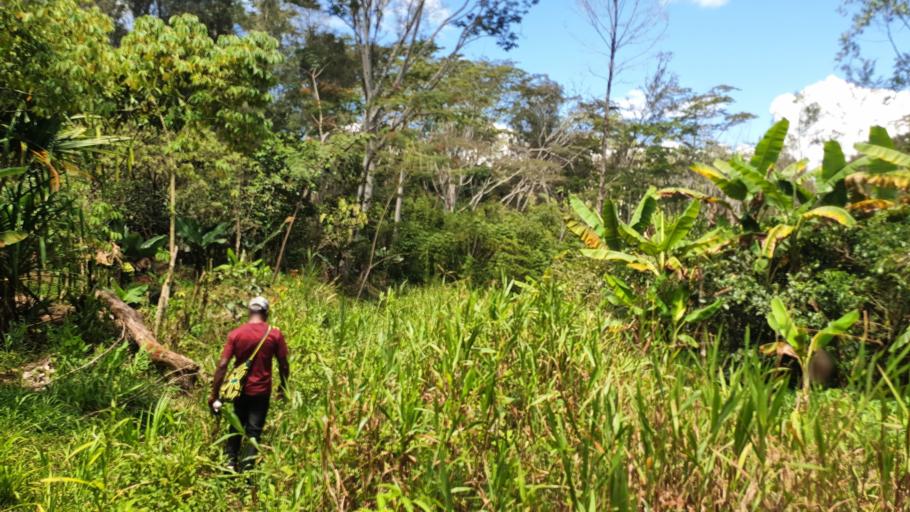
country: PG
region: Jiwaka
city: Minj
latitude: -5.9121
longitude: 144.8313
